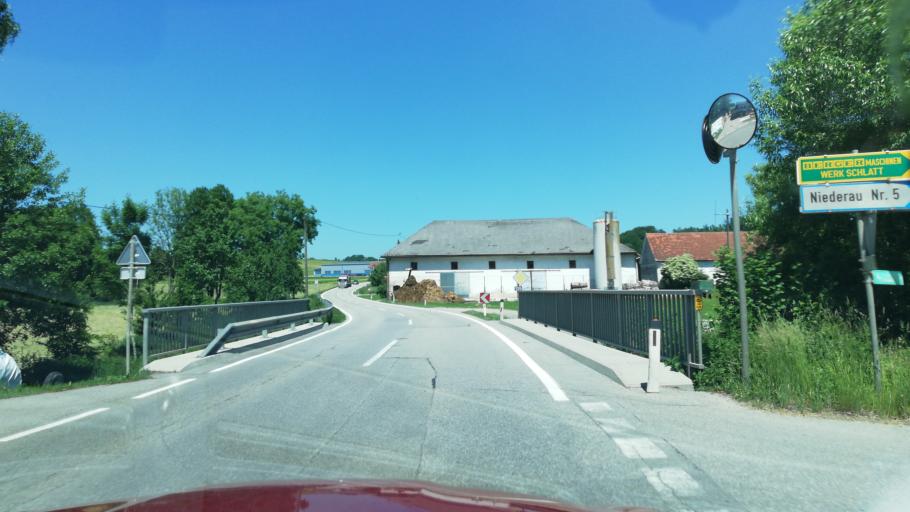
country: AT
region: Upper Austria
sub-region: Wels-Land
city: Aichkirchen
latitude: 48.0877
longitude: 13.7692
